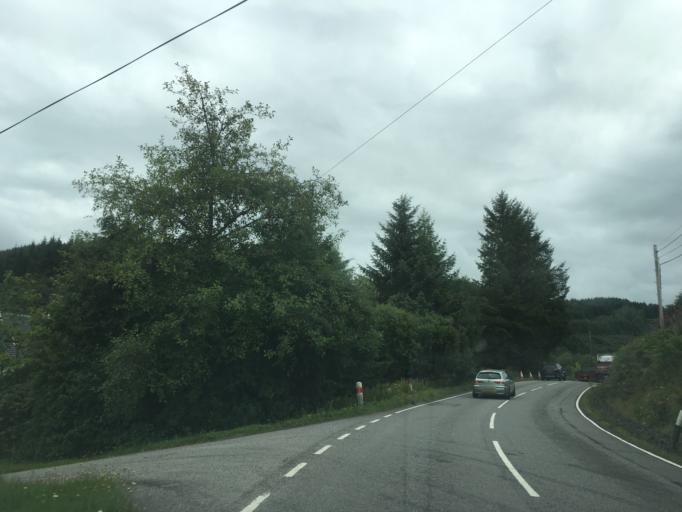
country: GB
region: Scotland
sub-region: Argyll and Bute
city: Oban
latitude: 56.2996
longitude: -5.4632
